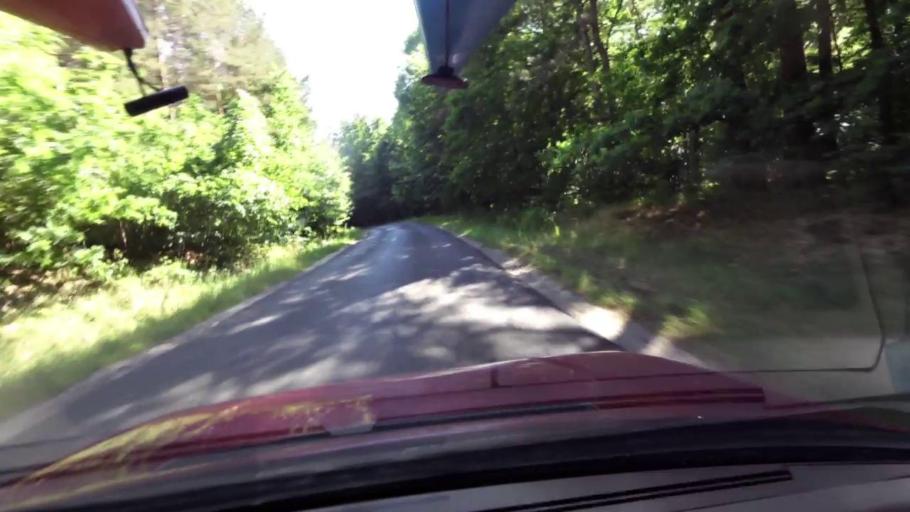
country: PL
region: Pomeranian Voivodeship
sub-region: Powiat slupski
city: Kepice
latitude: 54.2029
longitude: 16.8884
